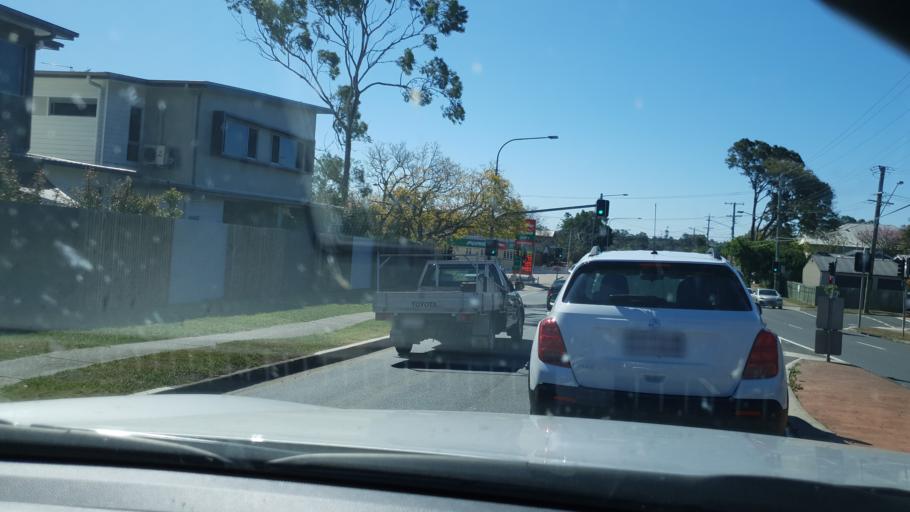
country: AU
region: Queensland
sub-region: Brisbane
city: Everton Park
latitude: -27.4259
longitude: 152.9901
